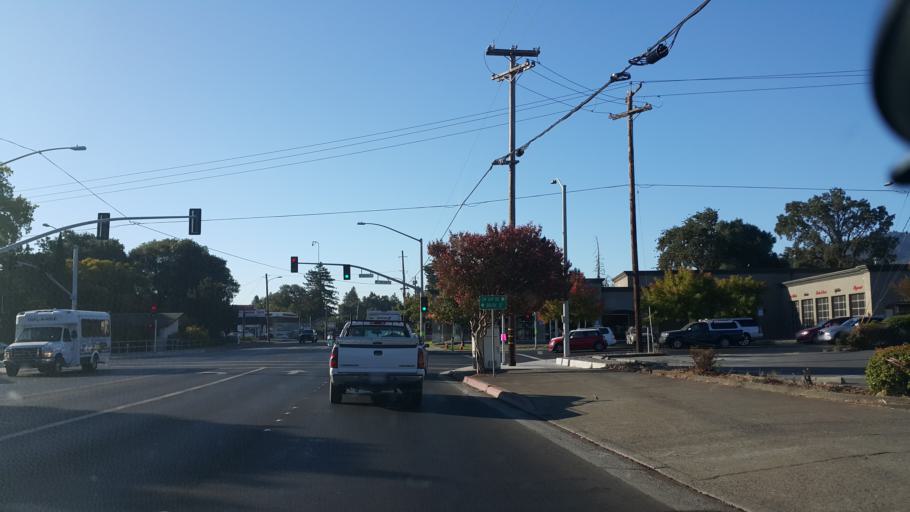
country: US
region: California
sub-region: Mendocino County
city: Ukiah
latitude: 39.1597
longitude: -123.2090
